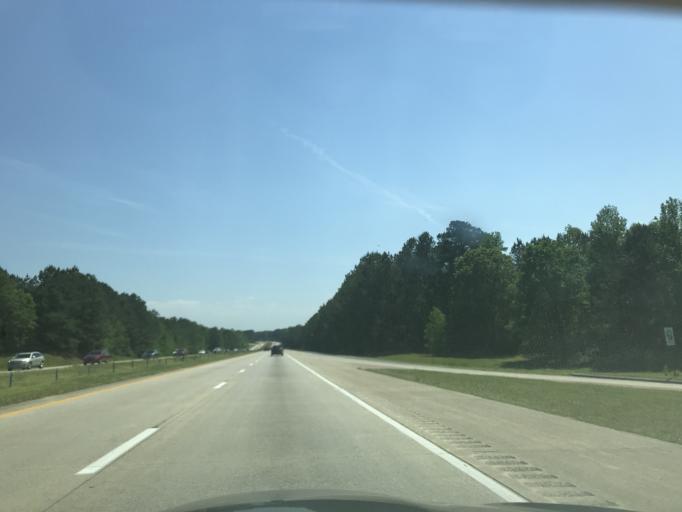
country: US
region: North Carolina
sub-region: Johnston County
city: Benson
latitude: 35.4342
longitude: -78.5331
